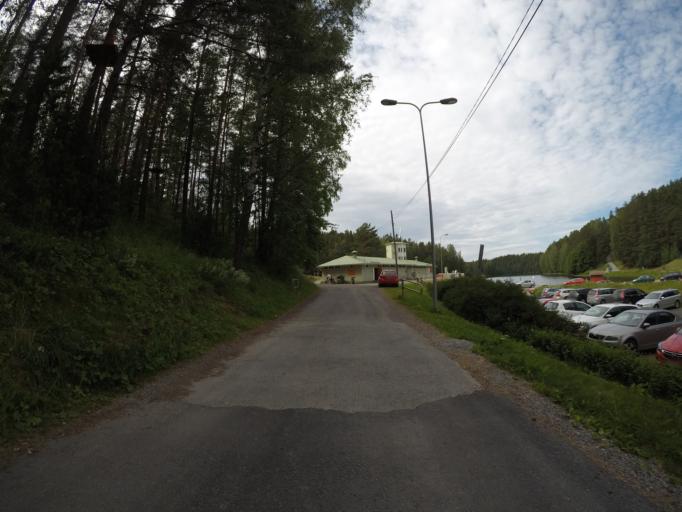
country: FI
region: Haeme
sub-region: Haemeenlinna
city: Haemeenlinna
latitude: 60.9921
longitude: 24.4216
